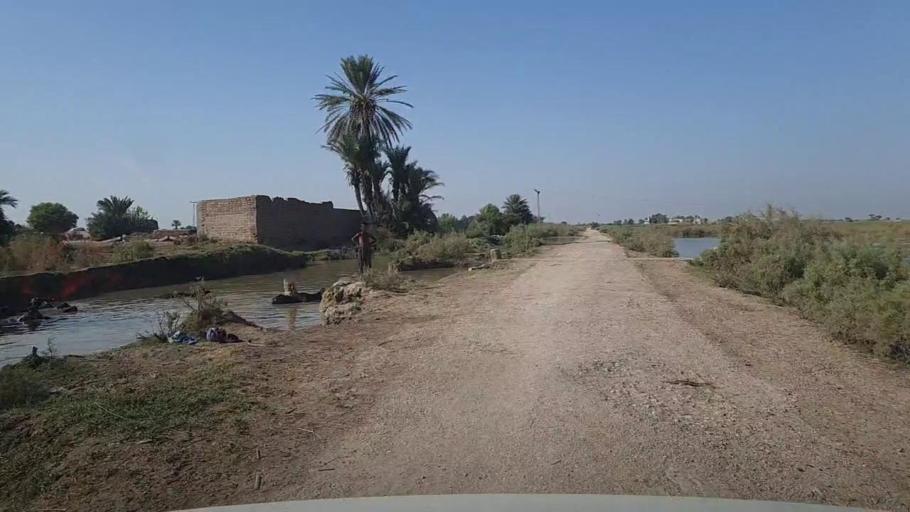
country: PK
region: Sindh
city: Kandhkot
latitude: 28.3793
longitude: 69.3562
